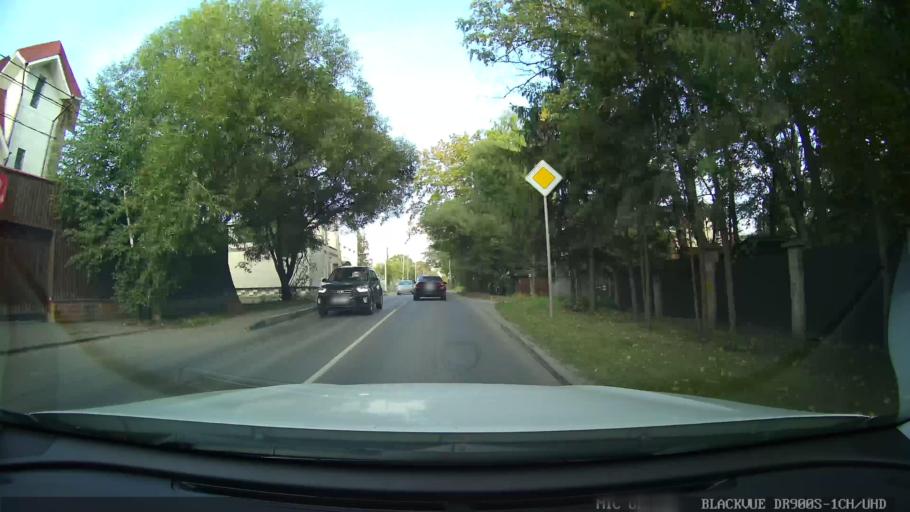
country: RU
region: Moskovskaya
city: Nemchinovka
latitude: 55.7235
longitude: 37.3651
